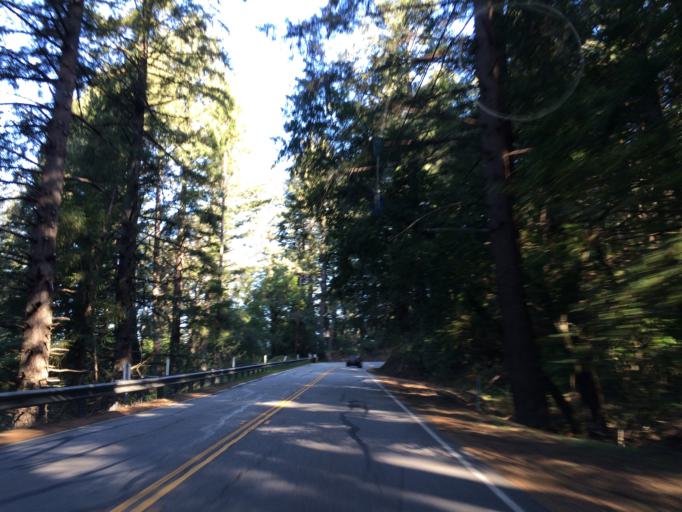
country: US
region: California
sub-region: Santa Cruz County
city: Boulder Creek
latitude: 37.2421
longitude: -122.1543
